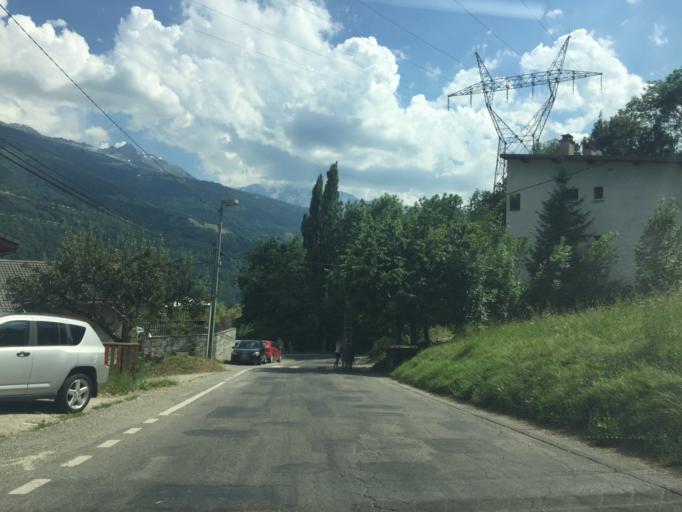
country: FR
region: Rhone-Alpes
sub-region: Departement de la Savoie
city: Bourg-Saint-Maurice
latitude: 45.6187
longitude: 6.7618
